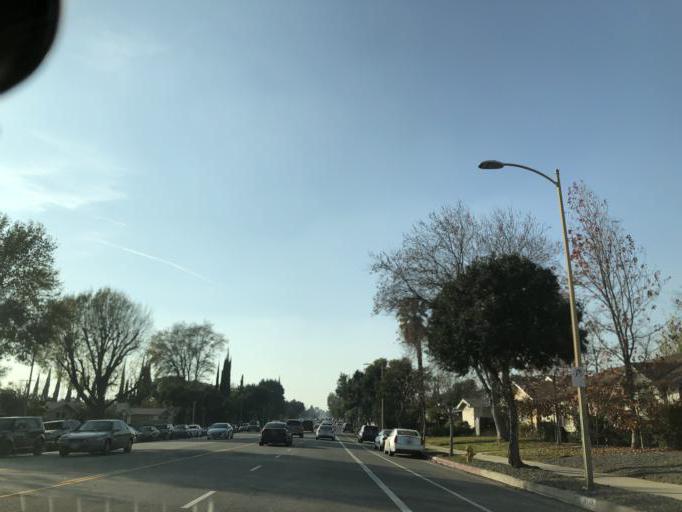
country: US
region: California
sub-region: Los Angeles County
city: Northridge
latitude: 34.2794
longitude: -118.5064
